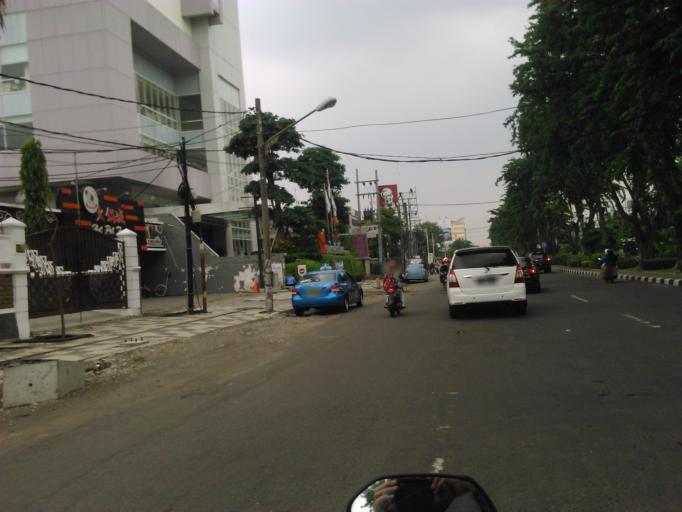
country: ID
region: East Java
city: Gubengairlangga
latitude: -7.2805
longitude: 112.7708
